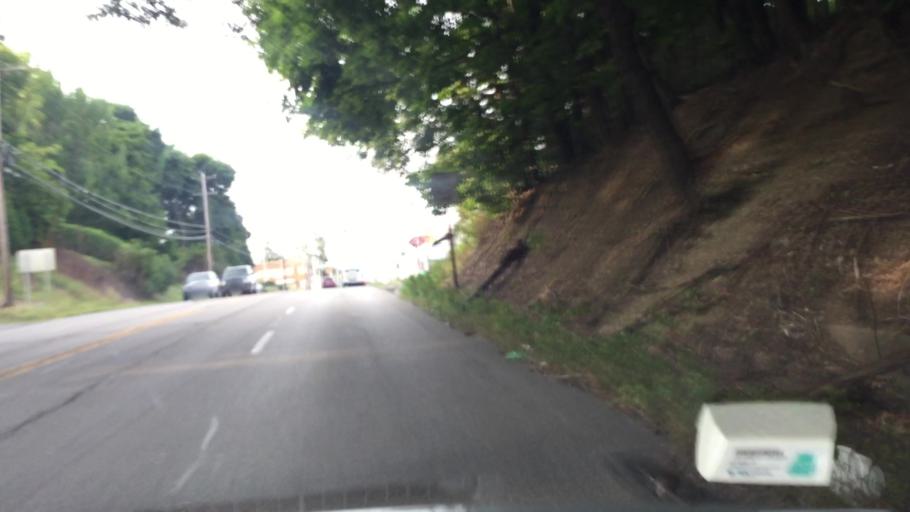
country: US
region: Pennsylvania
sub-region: Allegheny County
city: West View
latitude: 40.5431
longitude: -80.0360
